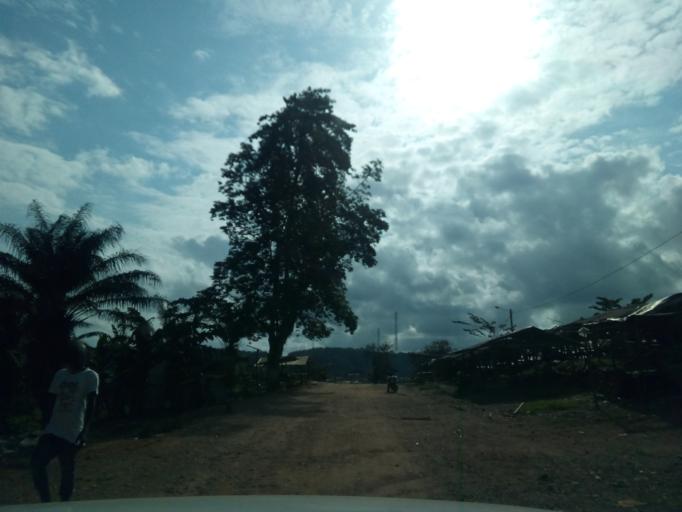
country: CI
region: Sud-Comoe
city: Mafere
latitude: 5.2918
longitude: -2.7908
